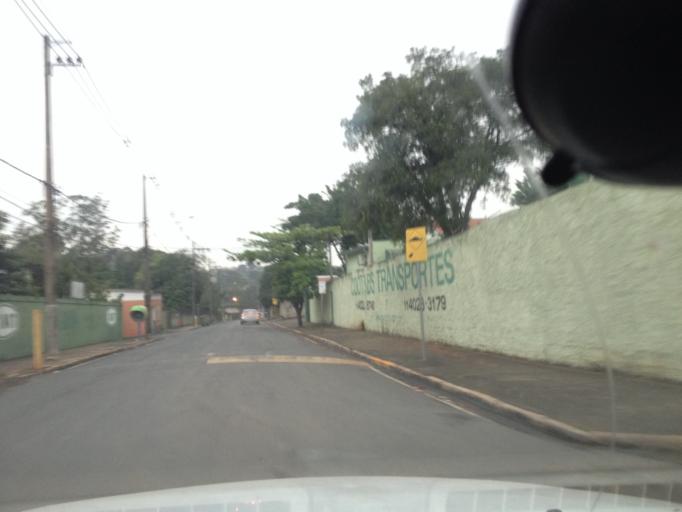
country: BR
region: Sao Paulo
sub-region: Salto
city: Salto
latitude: -23.2078
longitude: -47.2789
